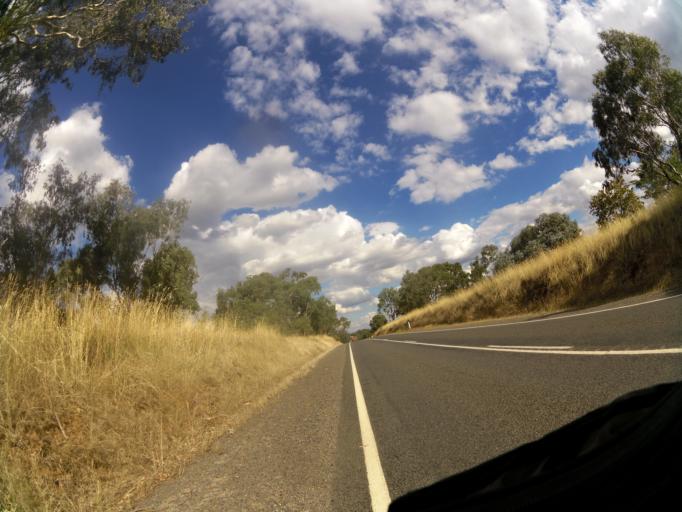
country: AU
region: Victoria
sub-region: Mansfield
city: Mansfield
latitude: -37.0152
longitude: 146.0884
